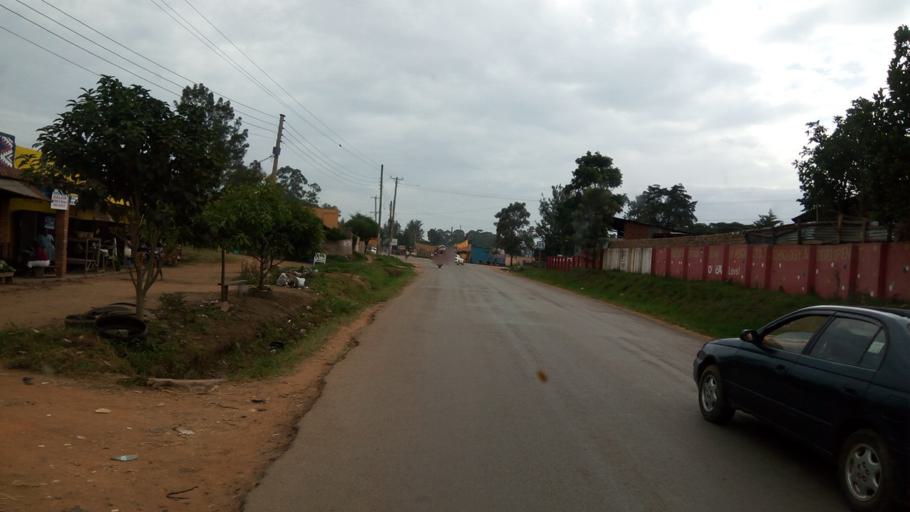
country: UG
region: Western Region
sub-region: Mbarara District
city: Mbarara
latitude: -0.6048
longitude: 30.6455
